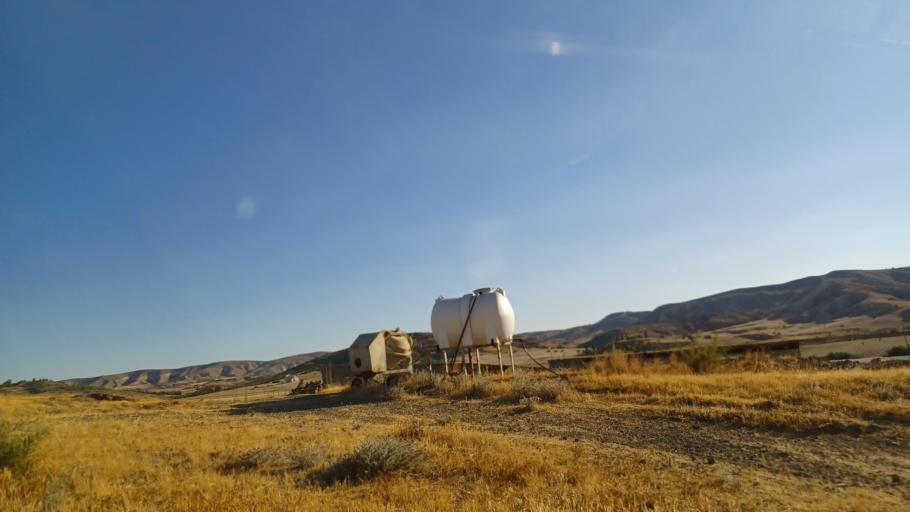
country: CY
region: Larnaka
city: Voroklini
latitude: 35.0066
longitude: 33.6391
